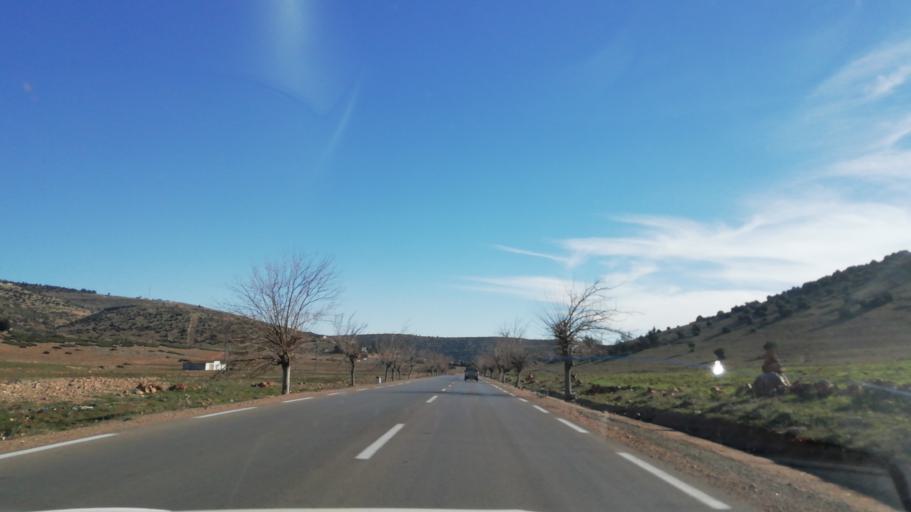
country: DZ
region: Tlemcen
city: Sebdou
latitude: 34.7115
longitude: -1.3233
